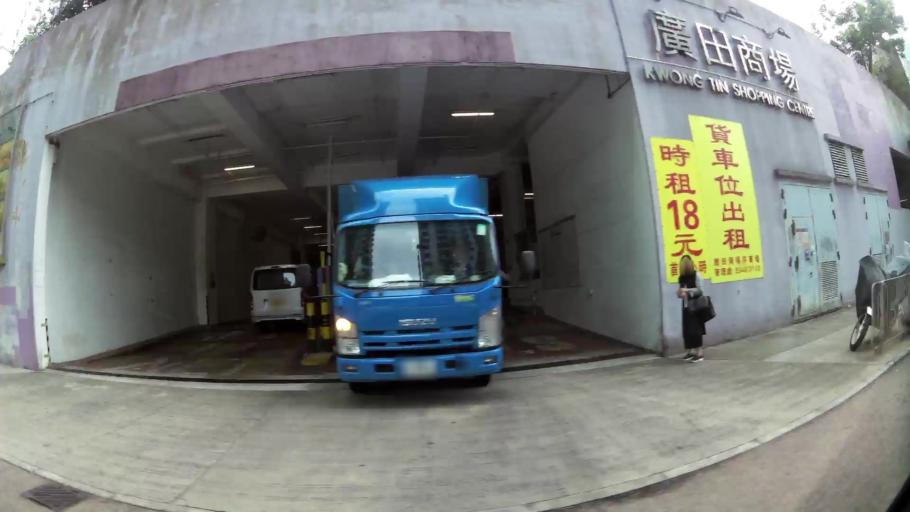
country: HK
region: Kowloon City
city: Kowloon
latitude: 22.3032
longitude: 114.2387
